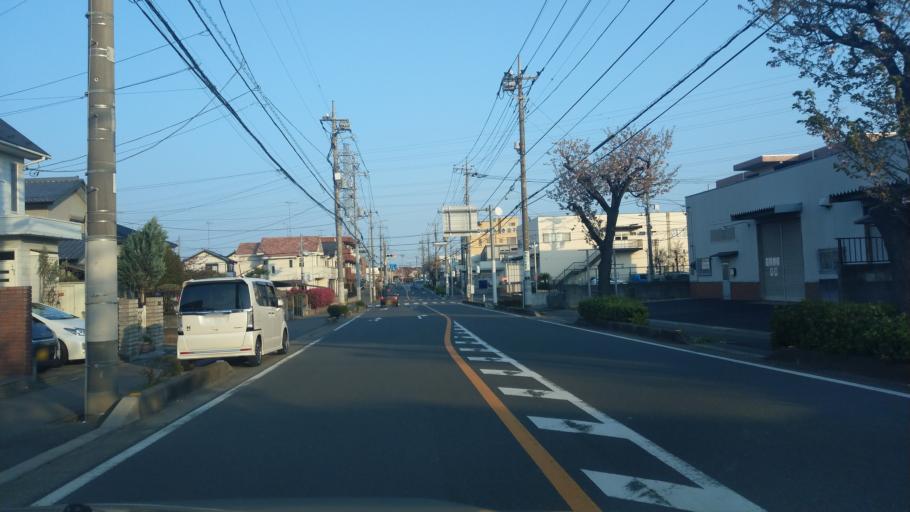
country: JP
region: Saitama
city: Ageoshimo
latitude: 36.0083
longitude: 139.6020
